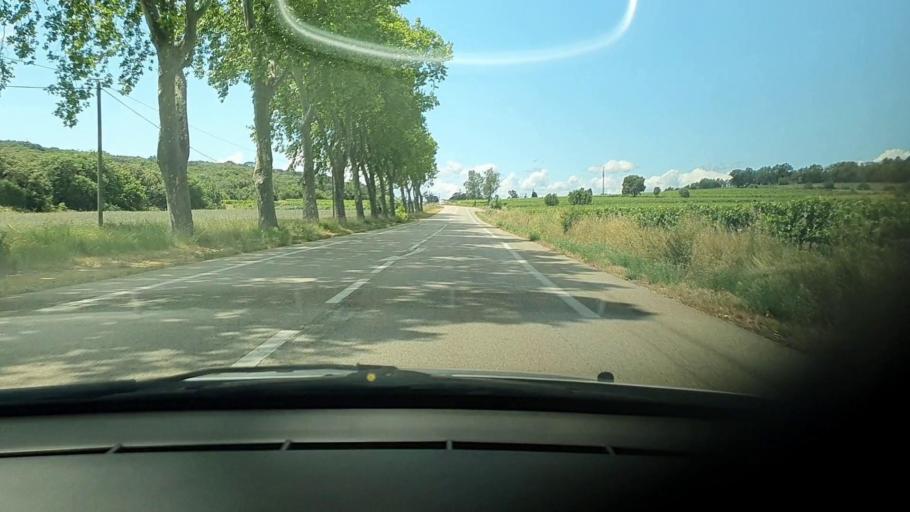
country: FR
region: Languedoc-Roussillon
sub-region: Departement du Gard
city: Saint-Chaptes
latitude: 44.0555
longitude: 4.2777
